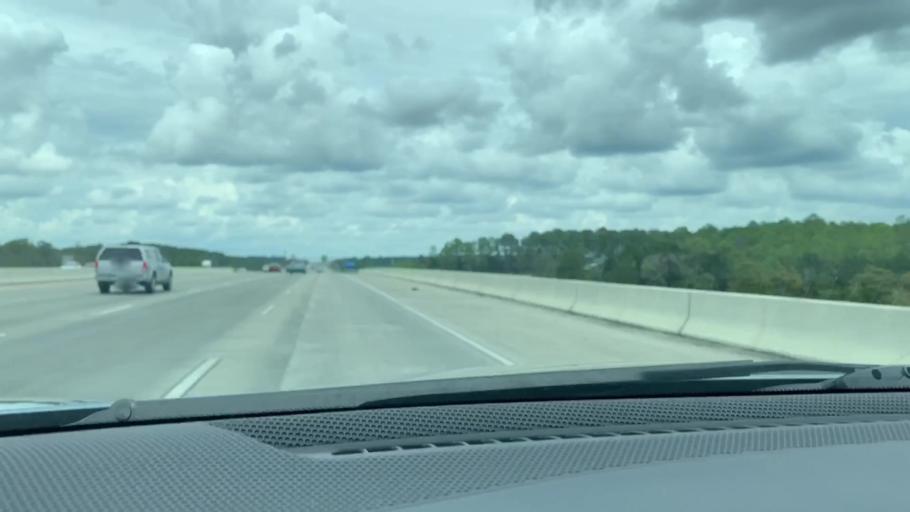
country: US
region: Georgia
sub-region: McIntosh County
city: Darien
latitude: 31.3728
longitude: -81.4549
